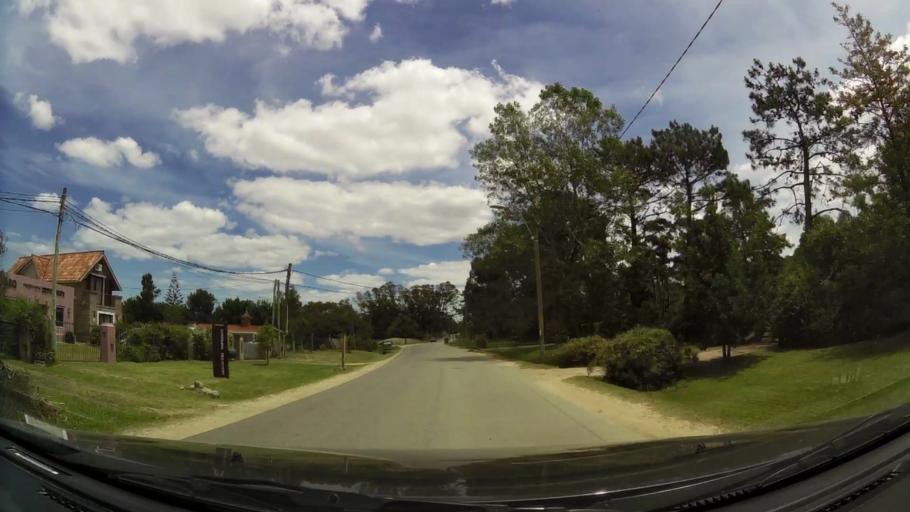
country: UY
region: Canelones
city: Empalme Olmos
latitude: -34.7979
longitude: -55.8894
